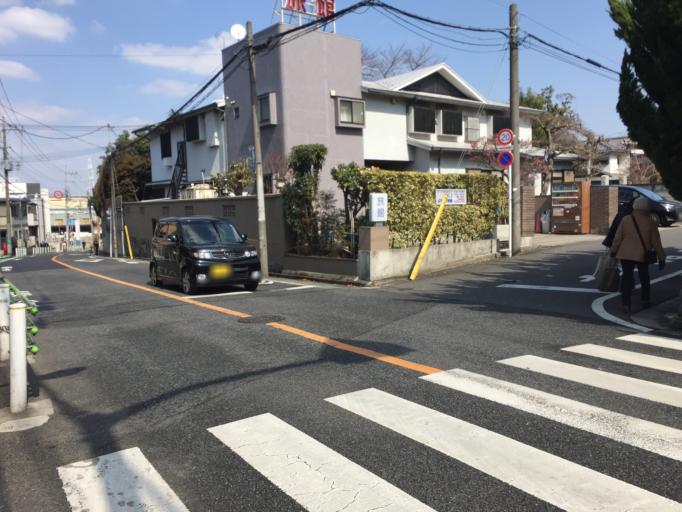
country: JP
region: Tokyo
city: Tokyo
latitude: 35.6681
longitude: 139.6415
